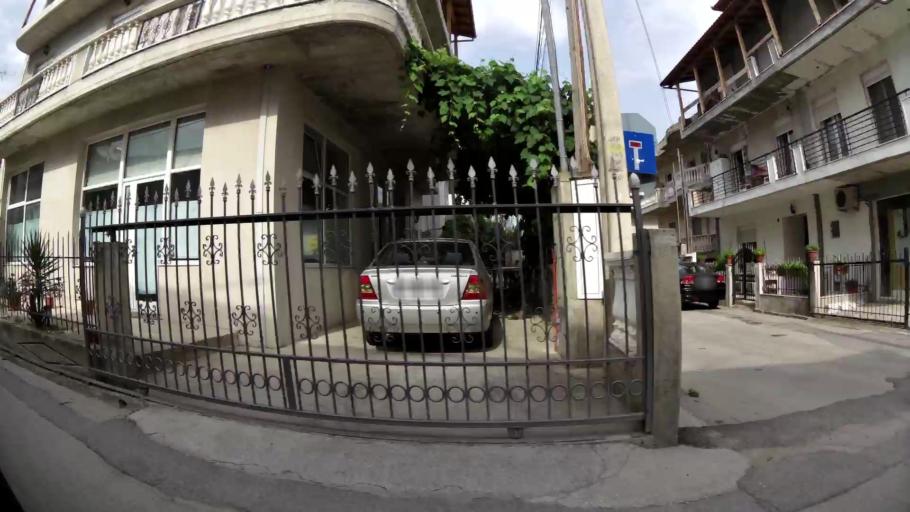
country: GR
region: Central Macedonia
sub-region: Nomos Thessalonikis
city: Stavroupoli
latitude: 40.6864
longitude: 22.9304
